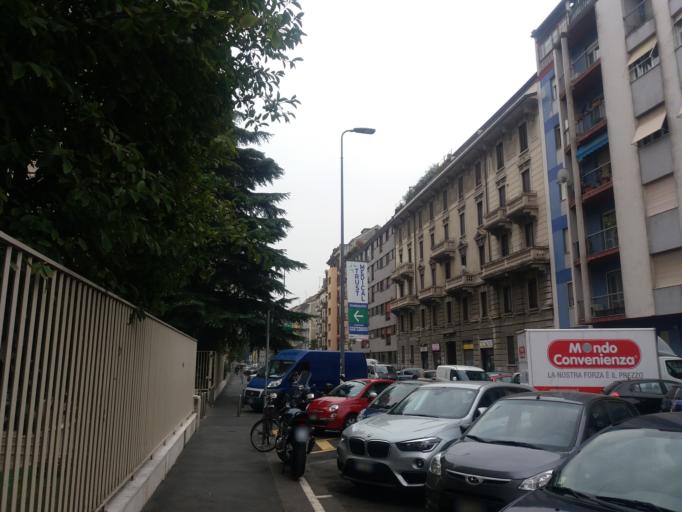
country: IT
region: Lombardy
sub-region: Citta metropolitana di Milano
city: Milano
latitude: 45.4835
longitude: 9.2251
